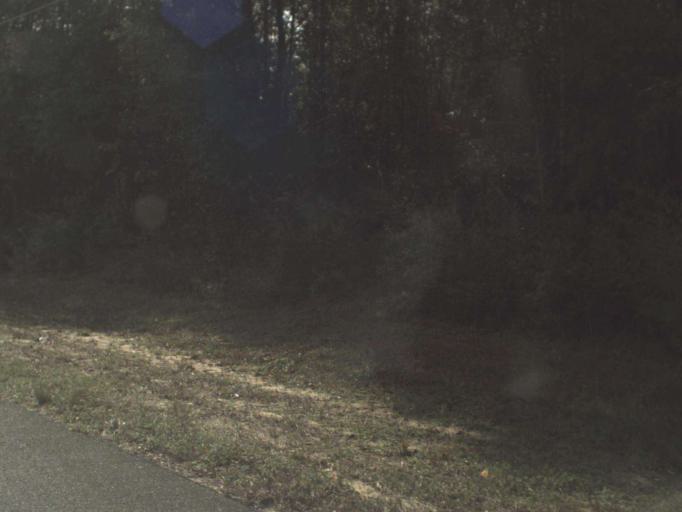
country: US
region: Florida
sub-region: Santa Rosa County
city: Point Baker
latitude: 30.7284
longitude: -87.0442
